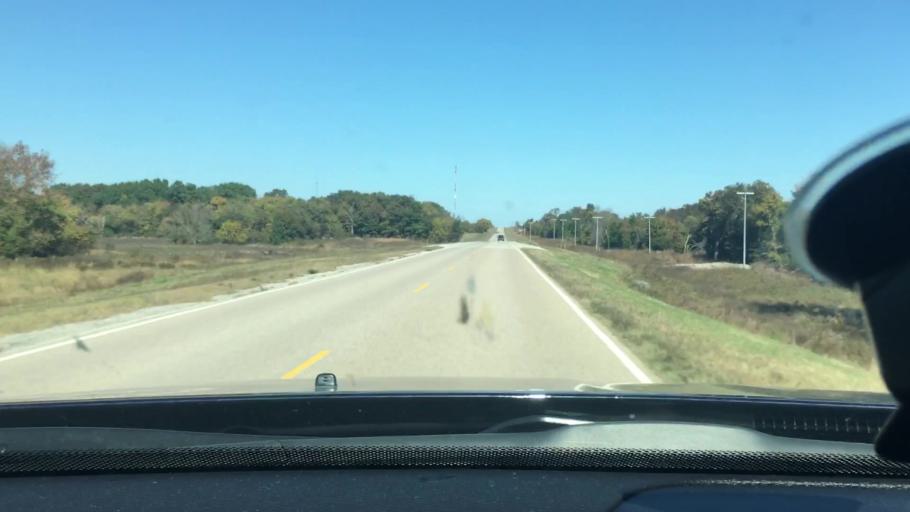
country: US
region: Oklahoma
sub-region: Johnston County
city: Tishomingo
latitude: 34.4201
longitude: -96.6359
